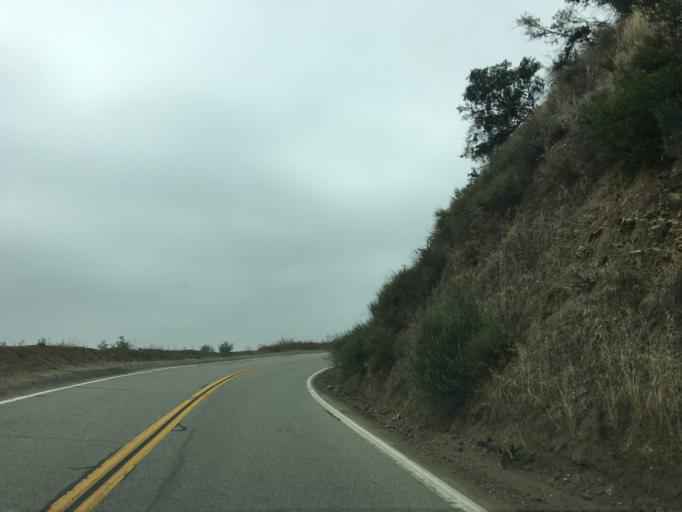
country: US
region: California
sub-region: Los Angeles County
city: Glendora
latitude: 34.1644
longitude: -117.8401
